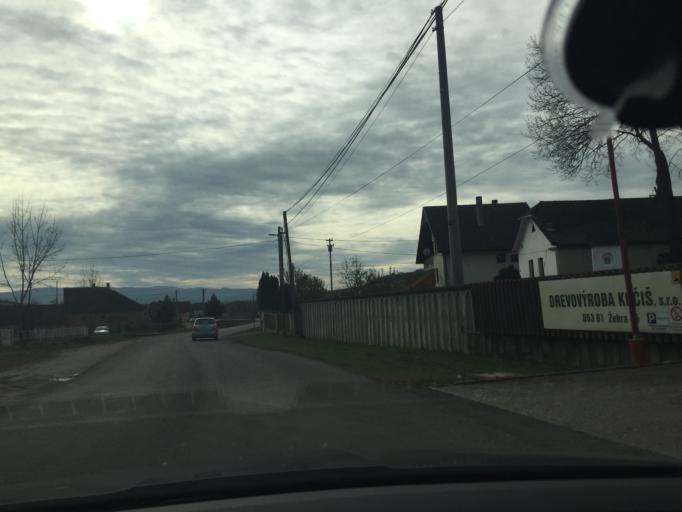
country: SK
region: Presovsky
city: Spisske Podhradie
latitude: 48.9821
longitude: 20.7928
